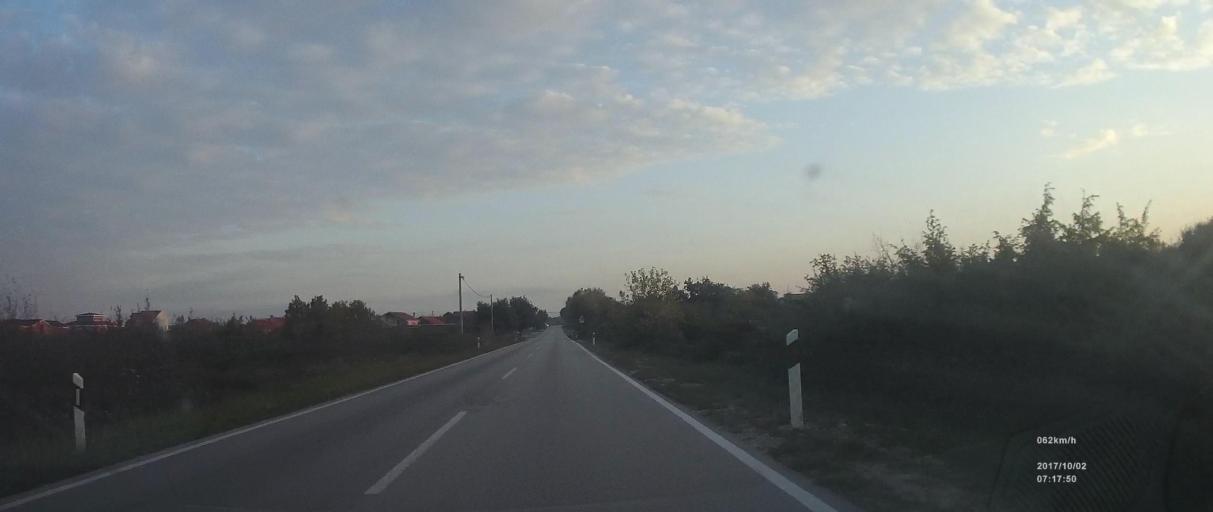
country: HR
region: Zadarska
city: Benkovac
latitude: 44.0130
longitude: 15.5933
